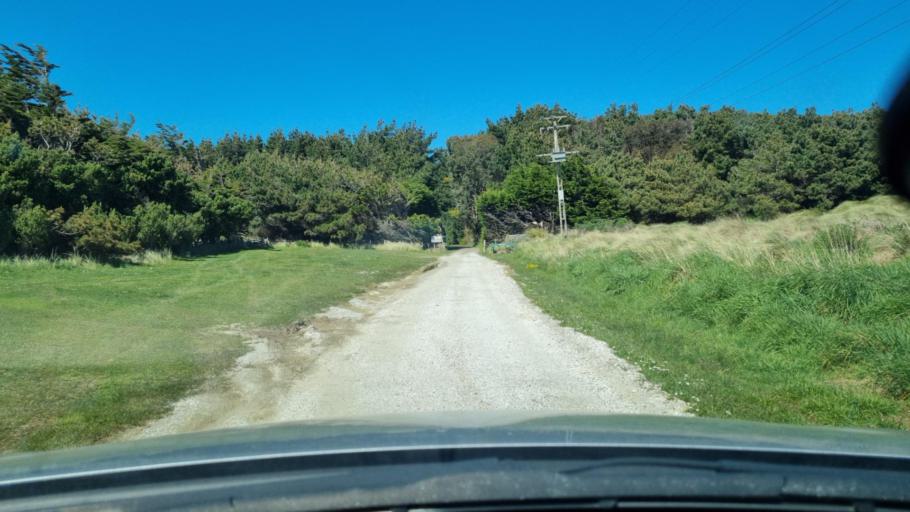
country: NZ
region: Southland
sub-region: Invercargill City
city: Invercargill
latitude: -46.4403
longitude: 168.2398
